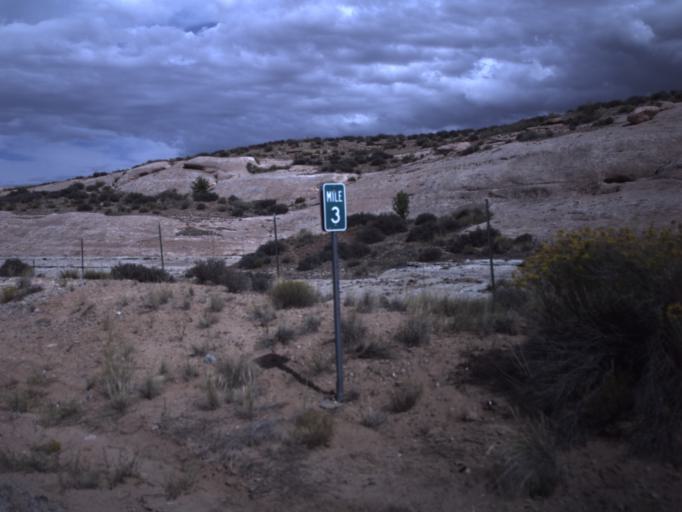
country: US
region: Utah
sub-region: San Juan County
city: Blanding
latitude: 37.2853
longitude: -109.4939
